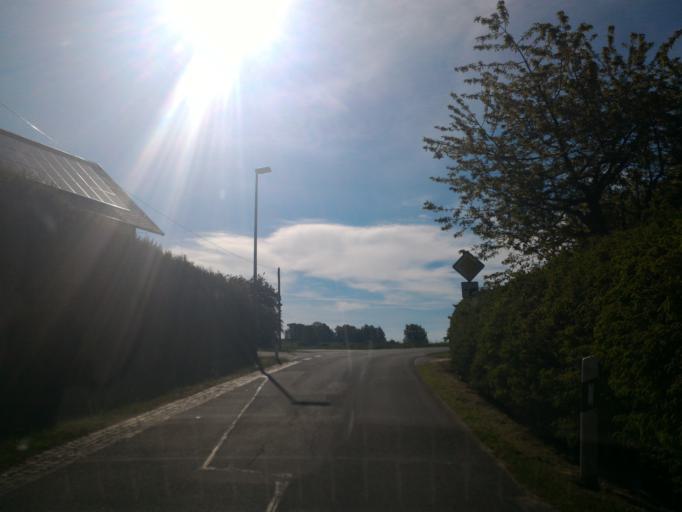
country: DE
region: Saxony
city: Grossschweidnitz
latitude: 51.0624
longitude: 14.6357
